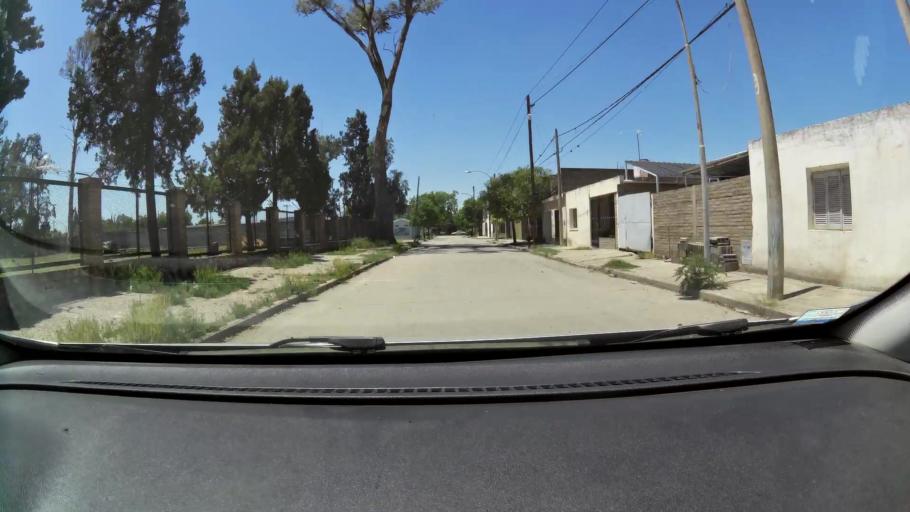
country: AR
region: Cordoba
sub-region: Departamento de Capital
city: Cordoba
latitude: -31.3834
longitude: -64.1296
